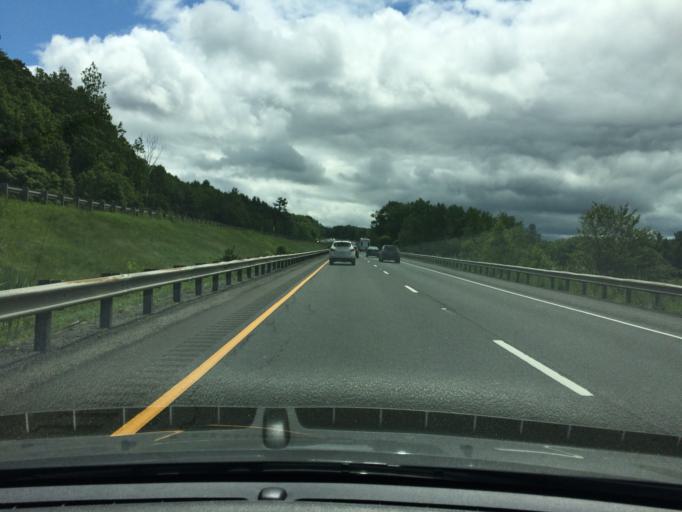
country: US
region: Massachusetts
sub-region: Berkshire County
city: Becket
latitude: 42.2662
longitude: -73.1301
